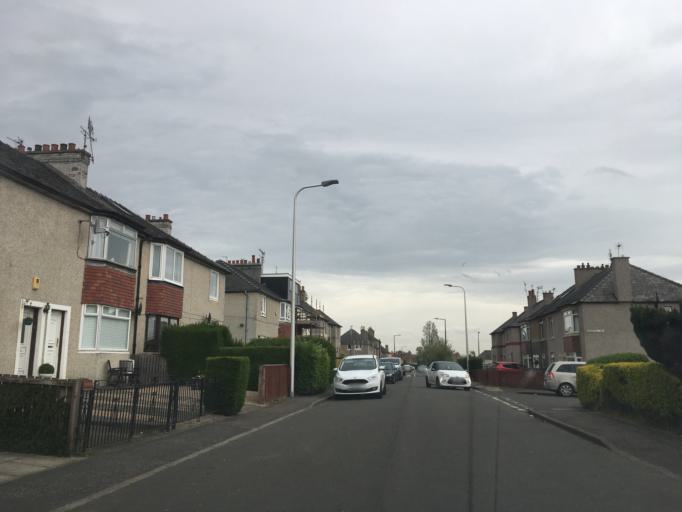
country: GB
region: Scotland
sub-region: Edinburgh
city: Colinton
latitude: 55.9224
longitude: -3.2851
